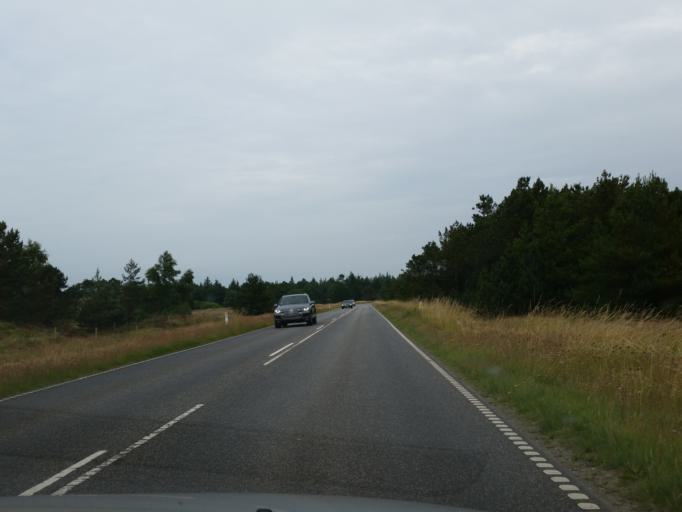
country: DE
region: Schleswig-Holstein
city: List
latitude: 55.1070
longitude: 8.5418
